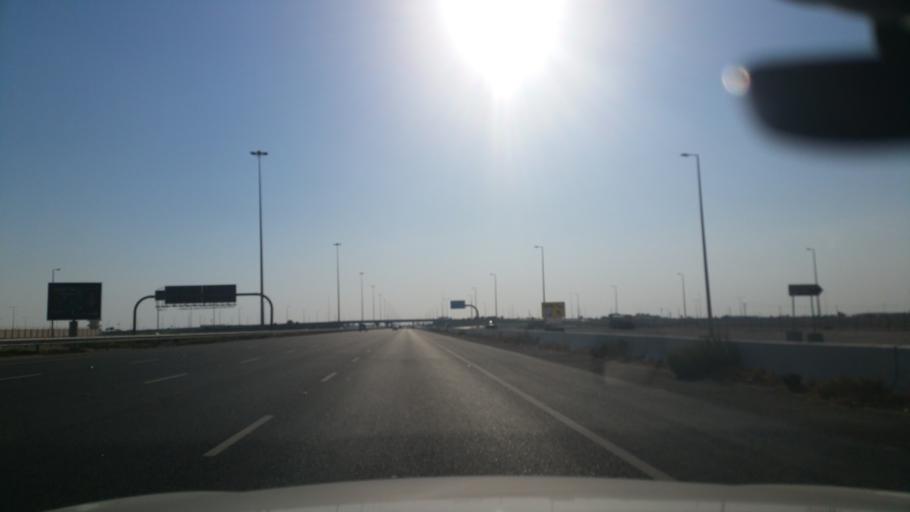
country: QA
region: Baladiyat ar Rayyan
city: Ar Rayyan
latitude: 25.2030
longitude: 51.3925
